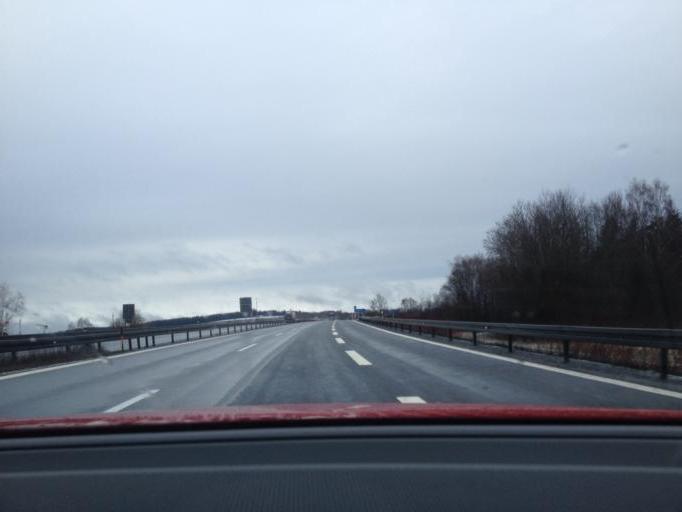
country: DE
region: Bavaria
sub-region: Upper Franconia
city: Selb
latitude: 50.1648
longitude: 12.1076
